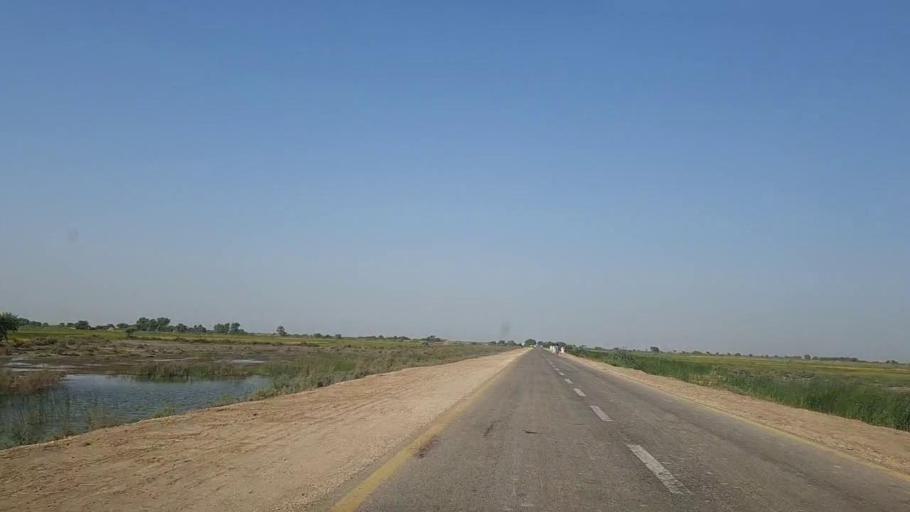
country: PK
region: Sindh
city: Jati
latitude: 24.4080
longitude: 68.2981
